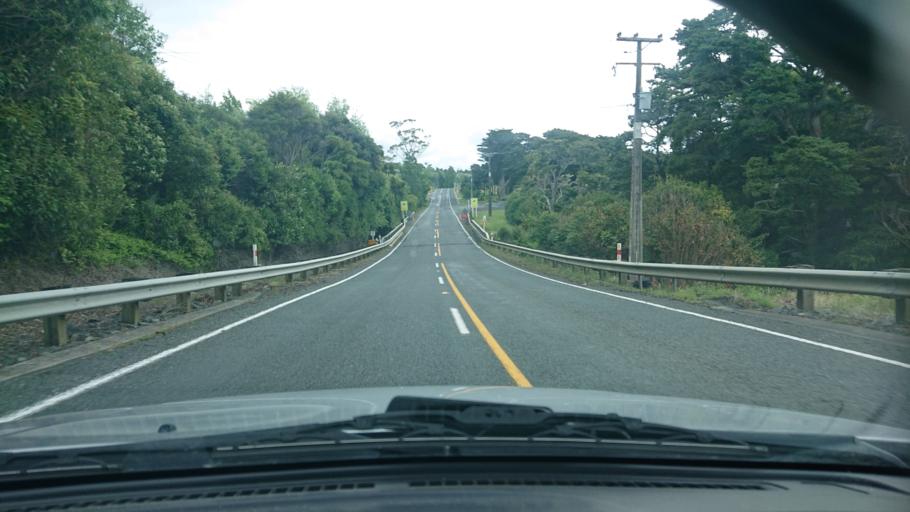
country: NZ
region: Auckland
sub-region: Auckland
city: Wellsford
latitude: -36.3755
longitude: 174.4539
